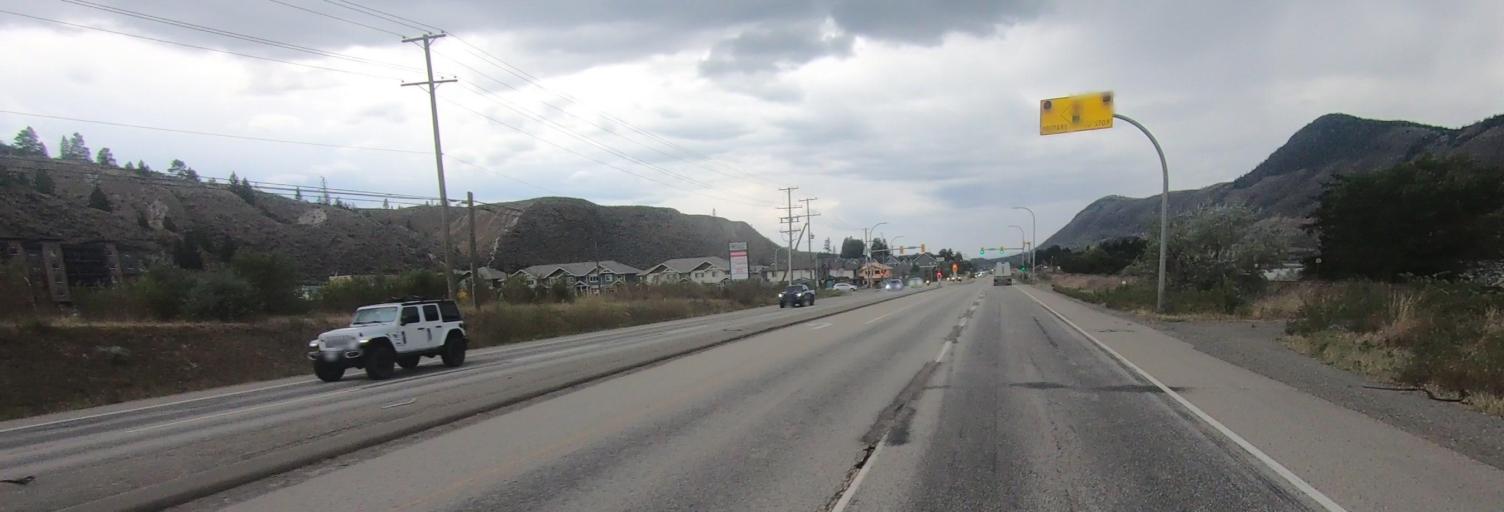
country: CA
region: British Columbia
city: Kamloops
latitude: 50.6716
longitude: -120.2244
